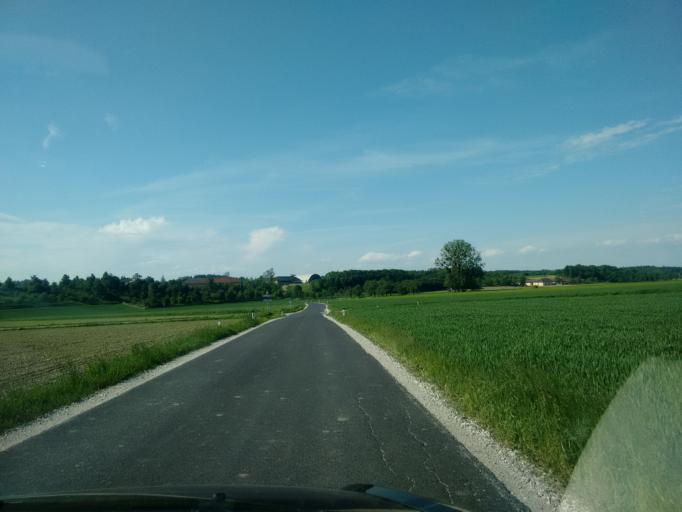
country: AT
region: Upper Austria
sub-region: Wels-Land
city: Gunskirchen
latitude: 48.1649
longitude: 13.9659
